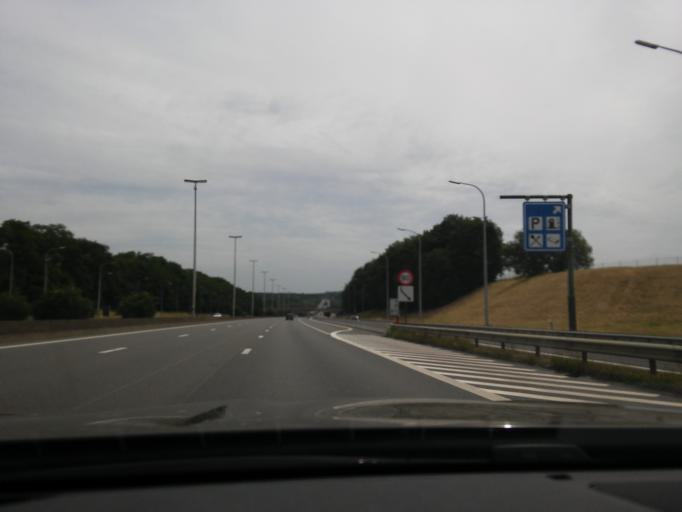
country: BE
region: Flanders
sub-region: Provincie Vlaams-Brabant
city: Bertem
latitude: 50.8562
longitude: 4.6449
